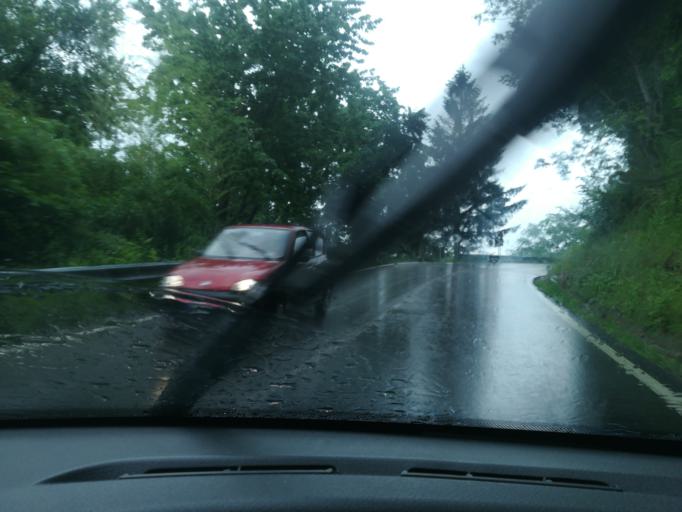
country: IT
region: The Marches
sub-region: Provincia di Macerata
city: Sarnano
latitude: 43.0119
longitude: 13.3268
